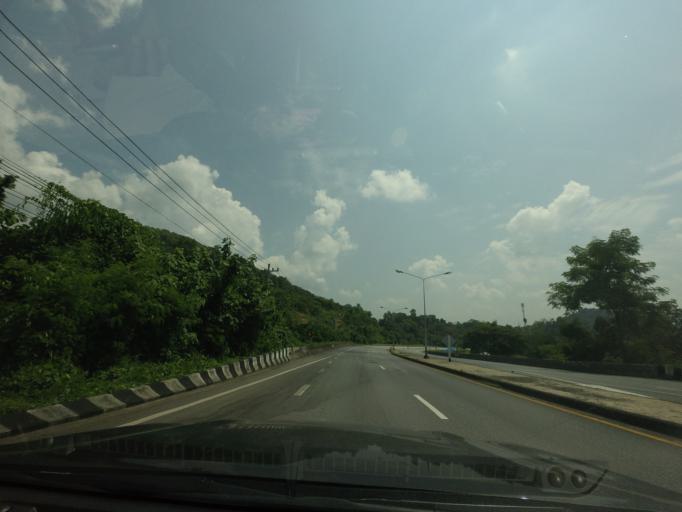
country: TH
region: Uttaradit
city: Lap Lae
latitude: 17.7764
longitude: 100.1288
